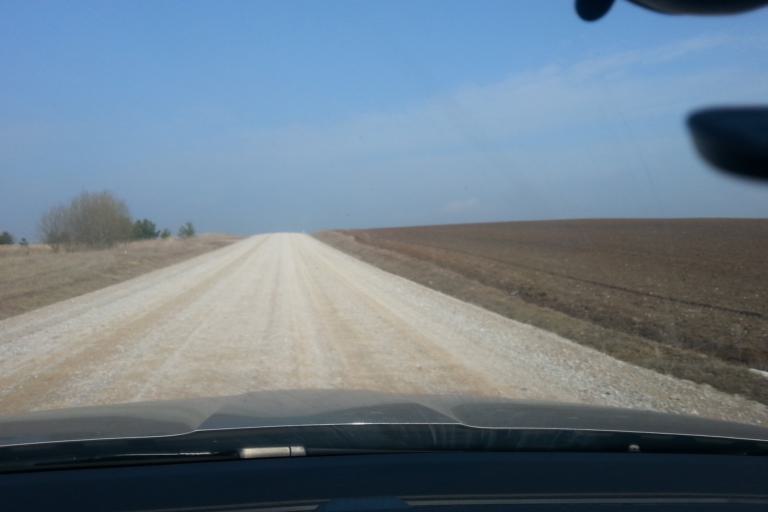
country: LT
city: Trakai
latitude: 54.5904
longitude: 24.9772
